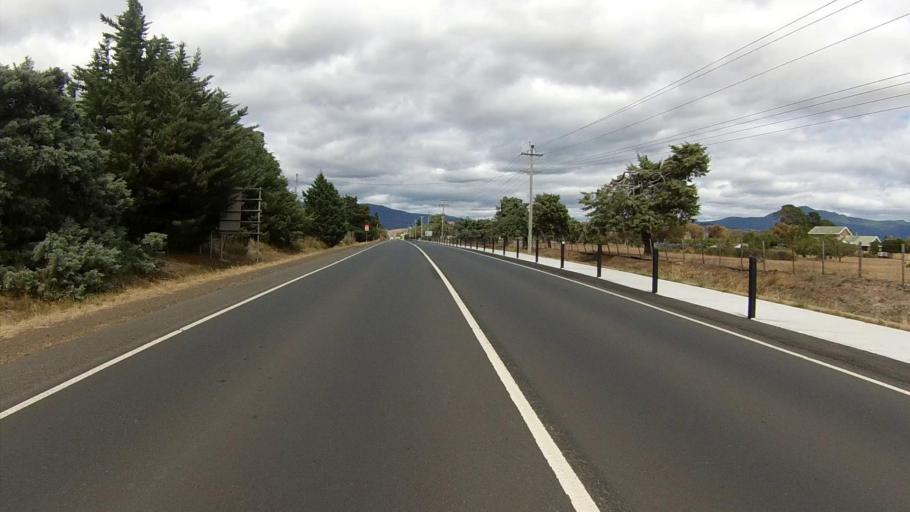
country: AU
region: Tasmania
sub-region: Brighton
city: Bridgewater
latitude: -42.6902
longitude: 147.2603
